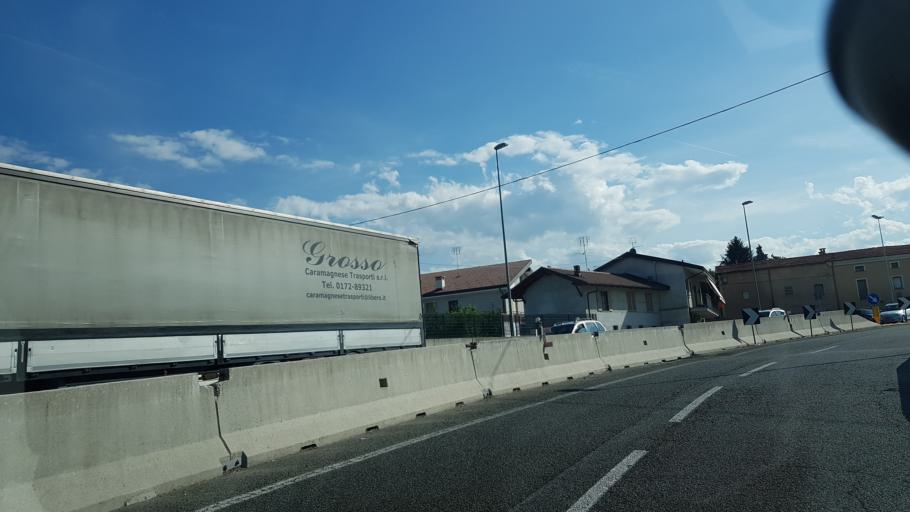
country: IT
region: Piedmont
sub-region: Provincia di Cuneo
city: Cuneo
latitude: 44.3890
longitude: 7.5827
